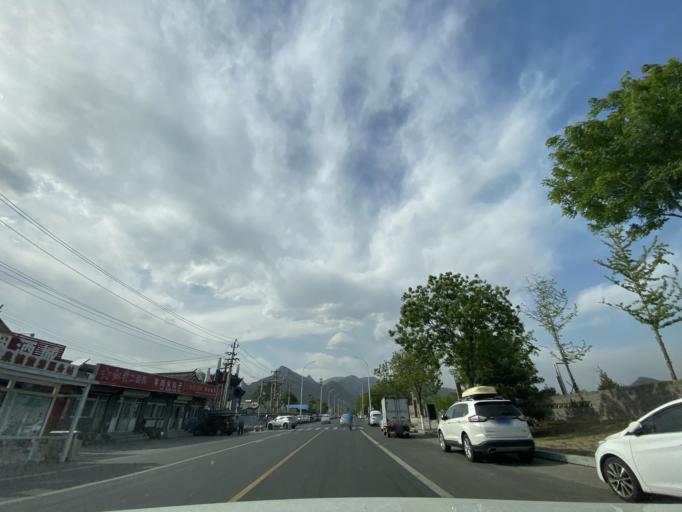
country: CN
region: Beijing
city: Junzhuang
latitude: 39.9820
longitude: 116.0820
